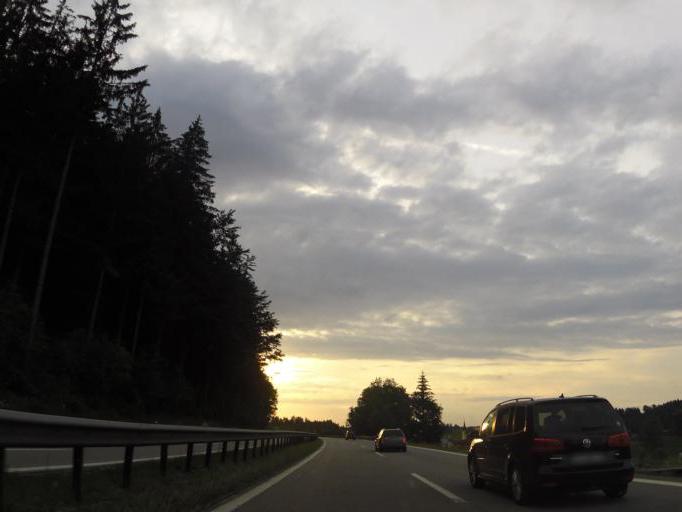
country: DE
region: Bavaria
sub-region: Upper Bavaria
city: Surberg
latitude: 47.8290
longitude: 12.7478
